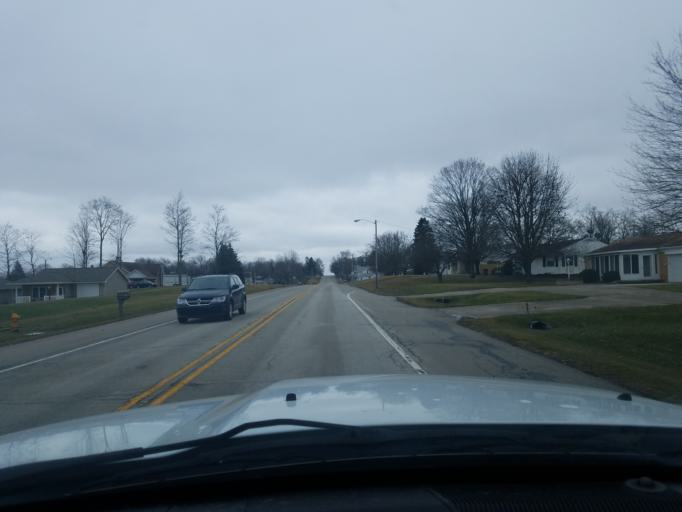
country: US
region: Indiana
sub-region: Noble County
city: Albion
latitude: 41.4039
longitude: -85.4239
